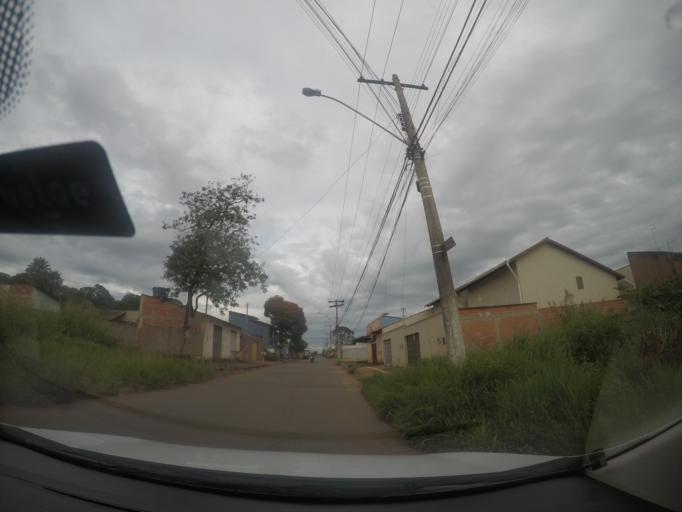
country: BR
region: Goias
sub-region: Goiania
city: Goiania
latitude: -16.5966
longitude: -49.3068
